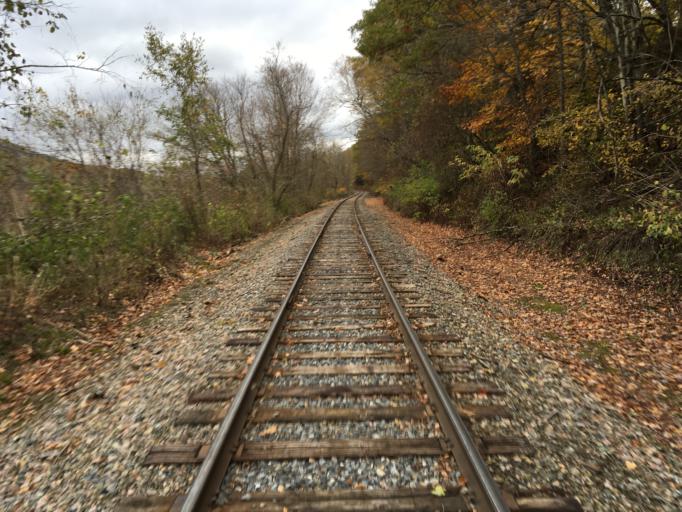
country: US
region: New Hampshire
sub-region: Grafton County
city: Woodsville
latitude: 44.1785
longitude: -72.0579
